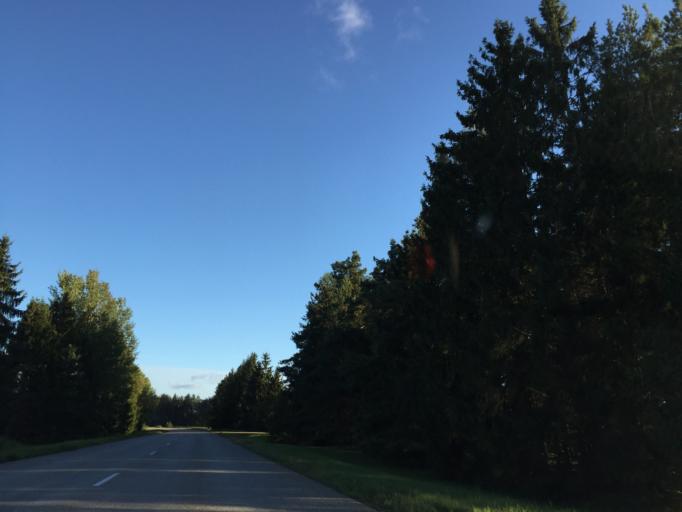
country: LV
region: Kuldigas Rajons
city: Kuldiga
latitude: 56.9167
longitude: 22.0547
